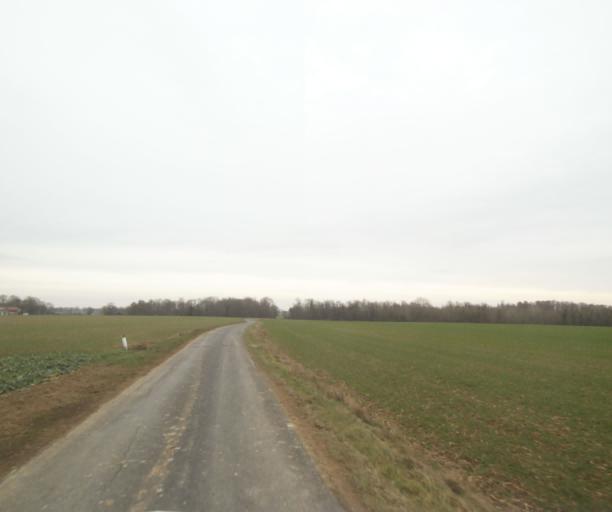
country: FR
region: Champagne-Ardenne
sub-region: Departement de la Haute-Marne
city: Villiers-en-Lieu
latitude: 48.6366
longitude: 4.8049
